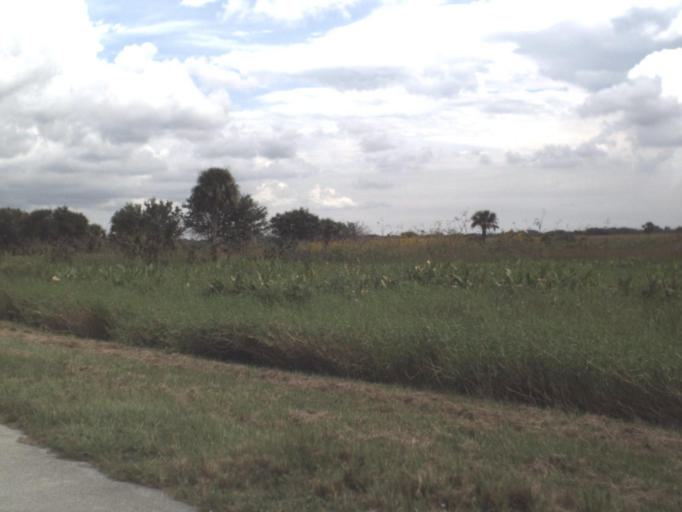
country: US
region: Florida
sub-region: Hendry County
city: Port LaBelle
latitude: 26.8478
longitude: -81.3823
